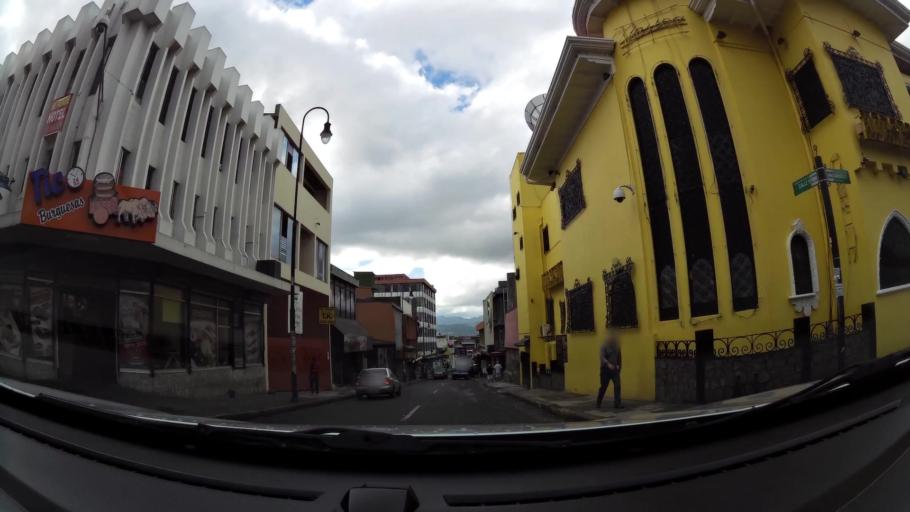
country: CR
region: San Jose
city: San Jose
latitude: 9.9344
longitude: -84.0747
